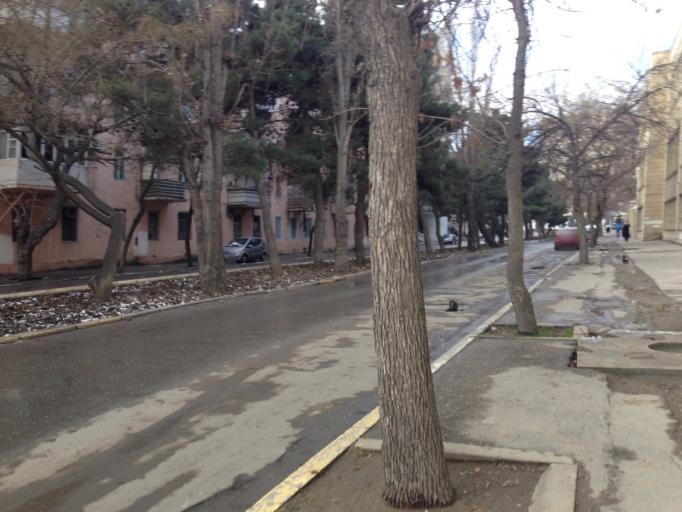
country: AZ
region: Baki
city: Baku
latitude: 40.3957
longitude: 49.8731
